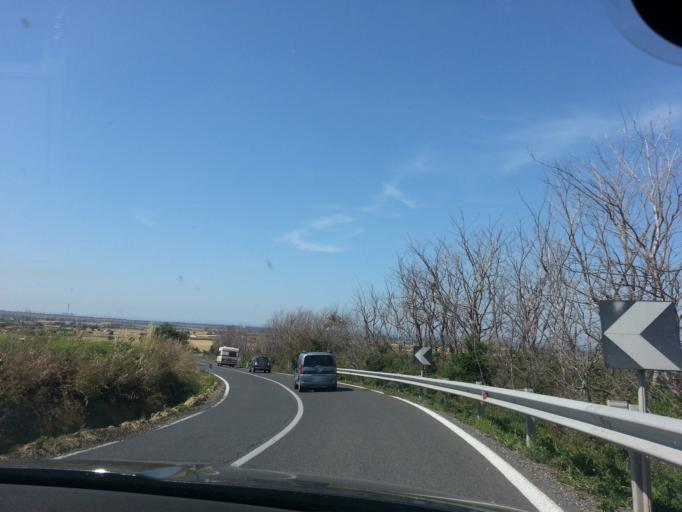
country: IT
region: Latium
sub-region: Provincia di Viterbo
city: Tarquinia
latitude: 42.2226
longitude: 11.7865
